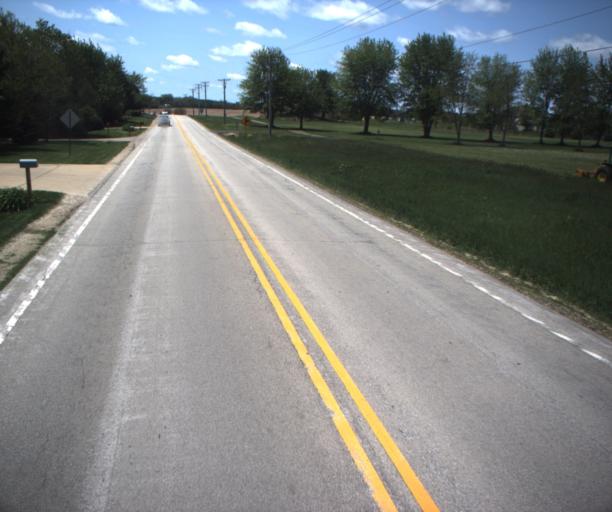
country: US
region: Illinois
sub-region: Kane County
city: Batavia
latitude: 41.8631
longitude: -88.3800
